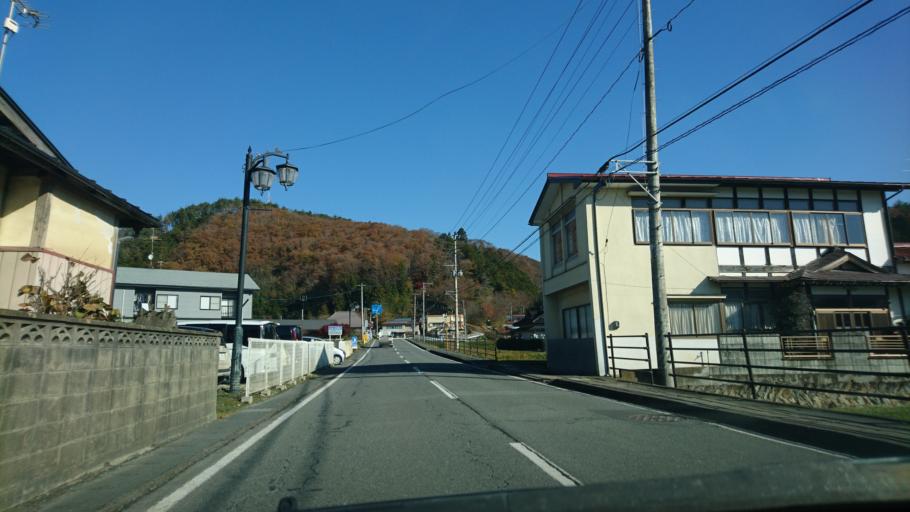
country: JP
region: Iwate
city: Ichinoseki
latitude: 38.9983
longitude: 141.2566
